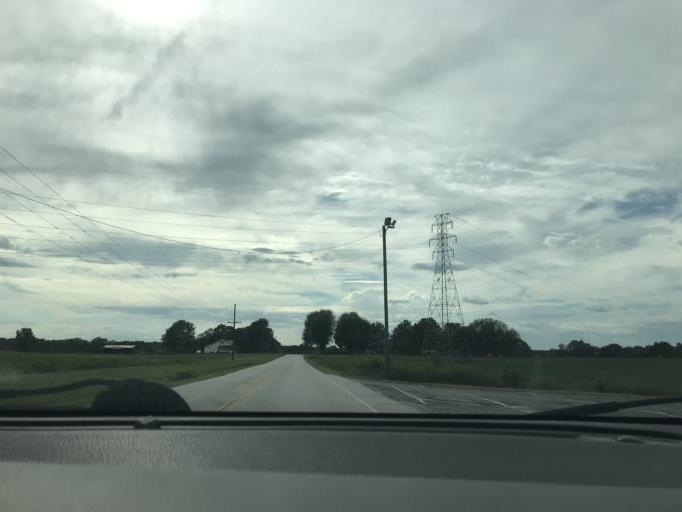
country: US
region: South Carolina
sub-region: Cherokee County
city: Gaffney
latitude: 35.1370
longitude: -81.6773
